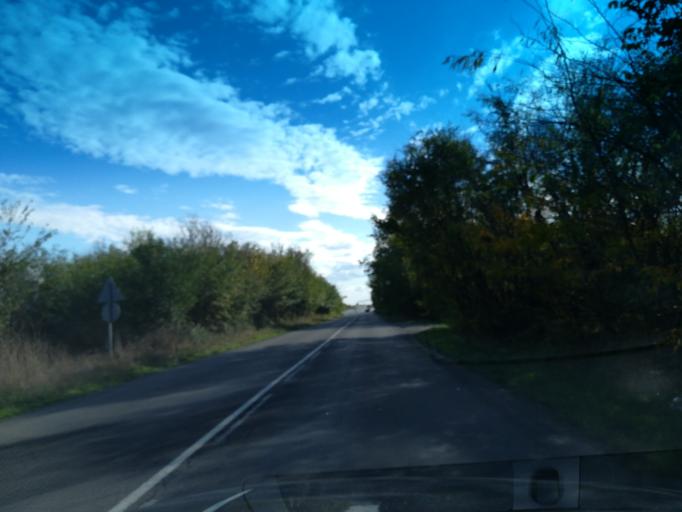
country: BG
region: Stara Zagora
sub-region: Obshtina Stara Zagora
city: Stara Zagora
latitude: 42.3477
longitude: 25.6595
